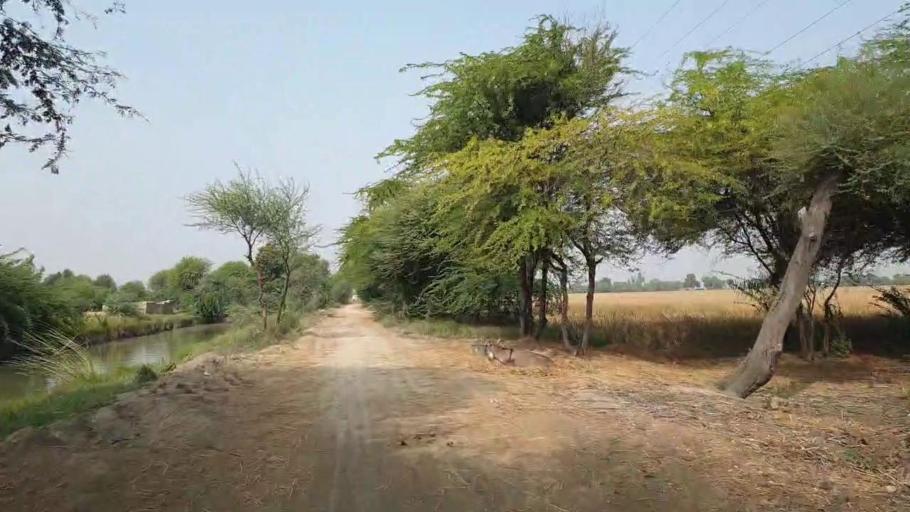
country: PK
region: Sindh
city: Kario
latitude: 24.8301
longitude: 68.5466
